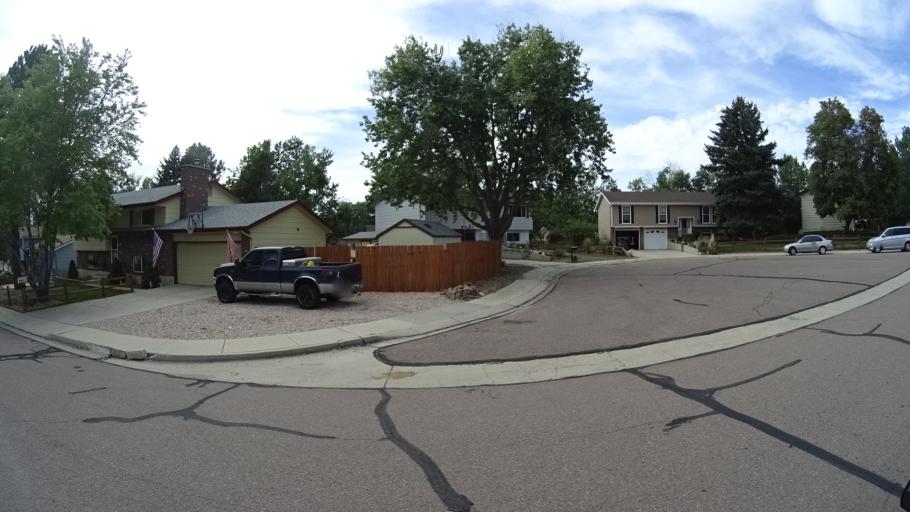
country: US
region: Colorado
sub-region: El Paso County
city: Colorado Springs
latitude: 38.9009
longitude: -104.7715
